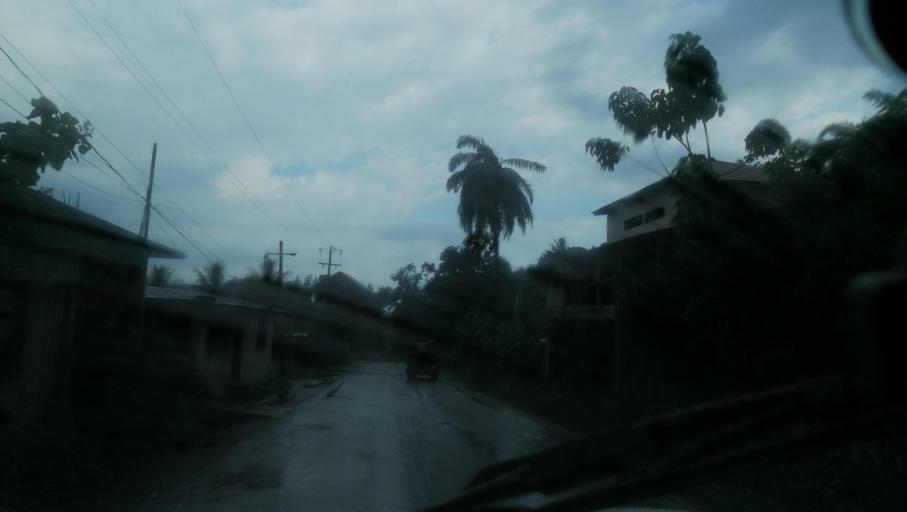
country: MX
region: Chiapas
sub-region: Cacahoatan
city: Benito Juarez
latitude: 15.0573
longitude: -92.1933
